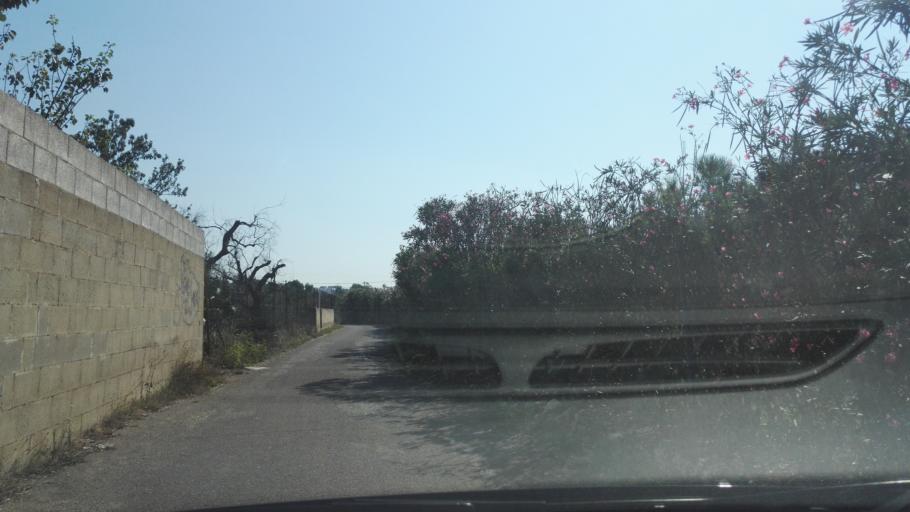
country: IT
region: Apulia
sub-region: Provincia di Lecce
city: Alezio
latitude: 40.0558
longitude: 18.0504
